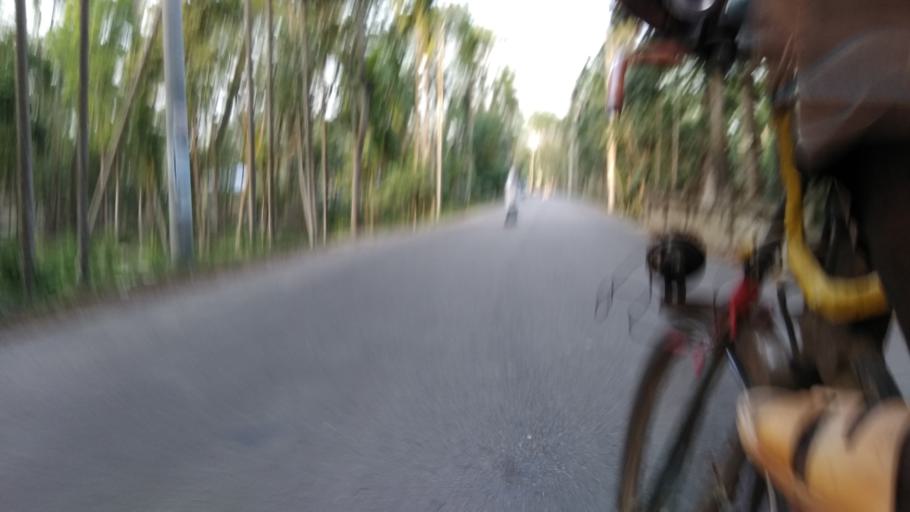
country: BD
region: Barisal
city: Mehendiganj
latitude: 22.9352
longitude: 90.4064
